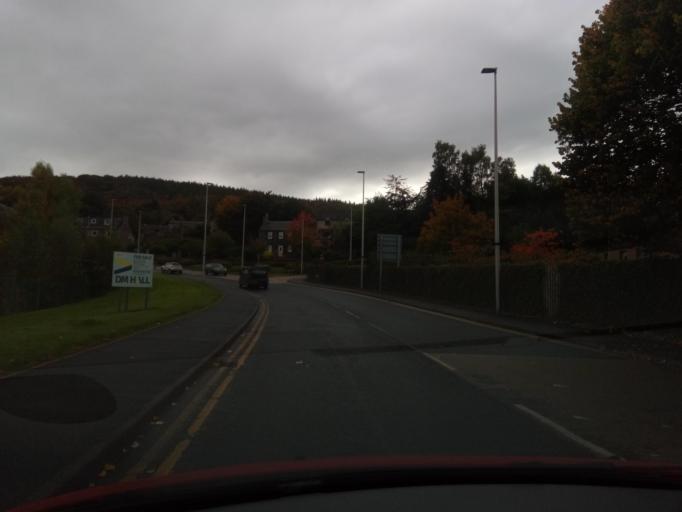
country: GB
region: Scotland
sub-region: The Scottish Borders
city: Galashiels
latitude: 55.6138
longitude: -2.8042
